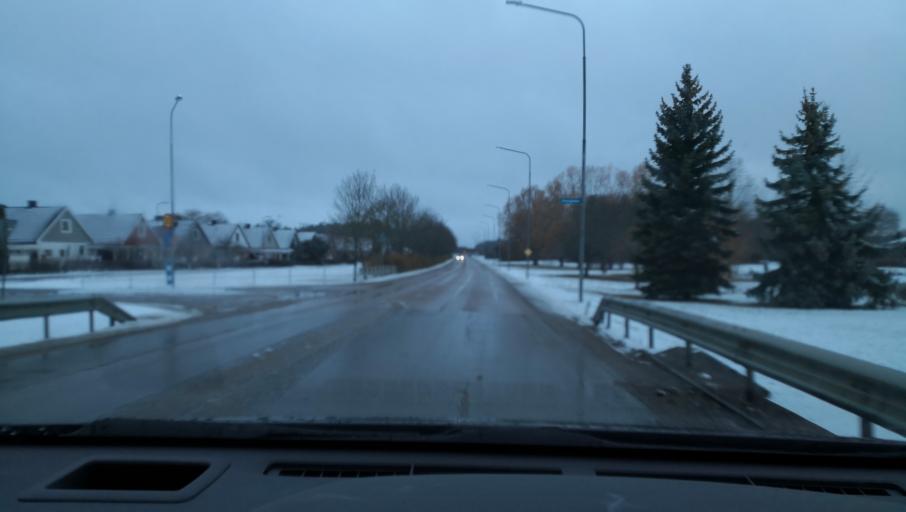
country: SE
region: Vaestmanland
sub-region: Kopings Kommun
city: Koping
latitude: 59.5168
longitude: 16.0116
